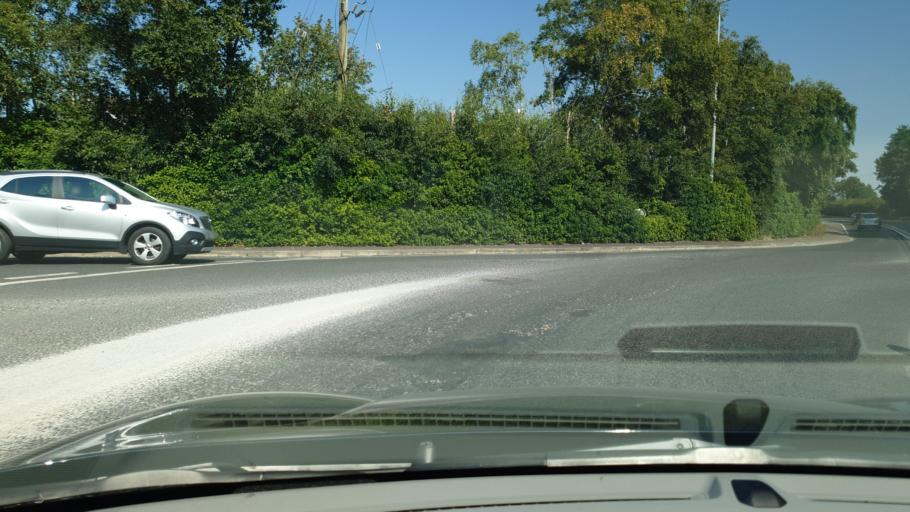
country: IE
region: Leinster
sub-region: An Mhi
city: Trim
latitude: 53.5475
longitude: -6.7943
